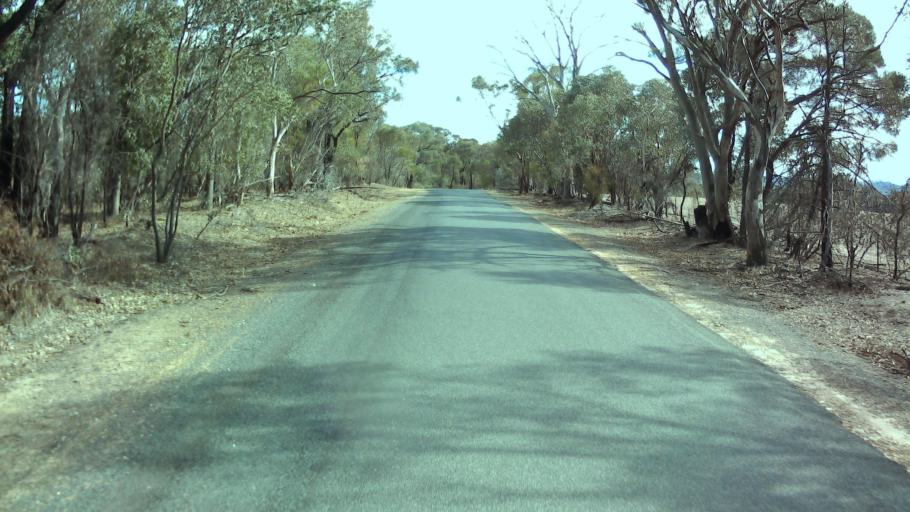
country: AU
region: New South Wales
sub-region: Weddin
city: Grenfell
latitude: -33.8740
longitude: 148.2018
